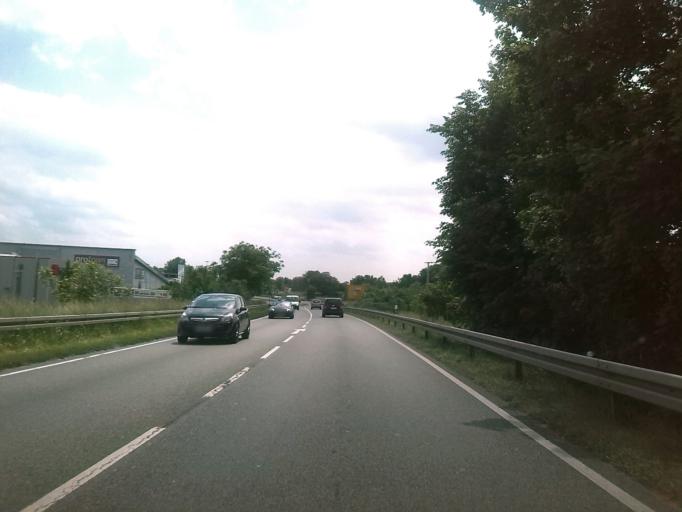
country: DE
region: Baden-Wuerttemberg
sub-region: Karlsruhe Region
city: Weinheim
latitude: 49.5600
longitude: 8.6489
